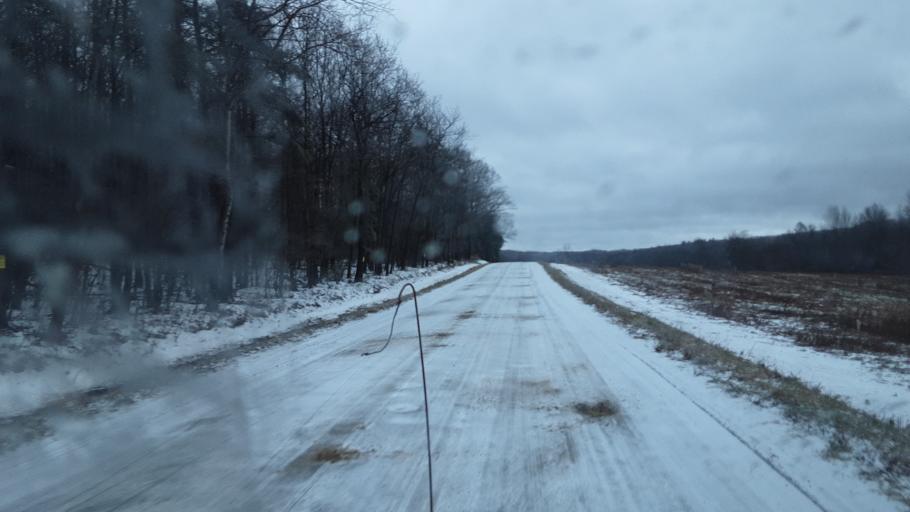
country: US
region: New York
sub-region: Allegany County
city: Friendship
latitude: 42.2814
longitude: -78.1623
